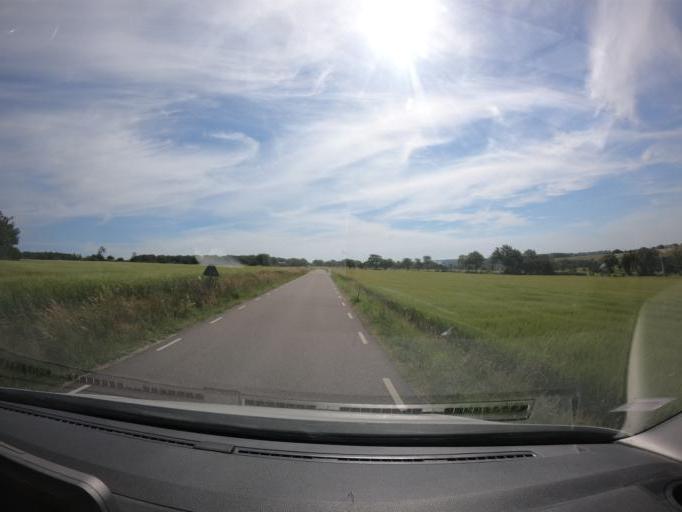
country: SE
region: Skane
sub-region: Bastads Kommun
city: Bastad
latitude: 56.4152
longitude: 12.7798
